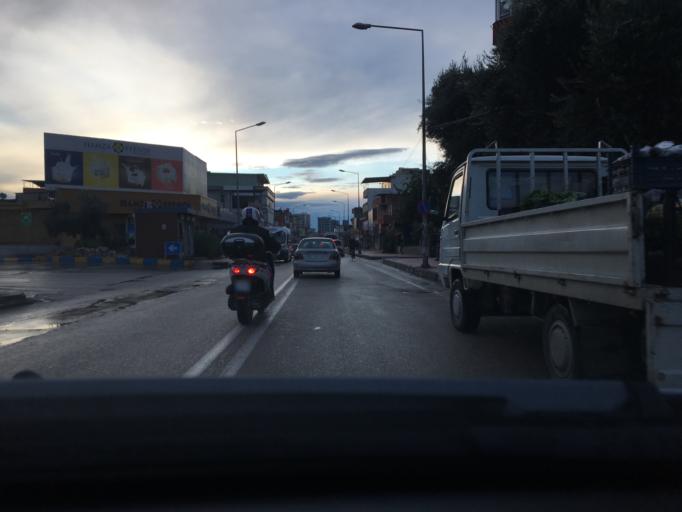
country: TR
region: Adana
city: Seyhan
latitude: 37.0205
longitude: 35.2950
